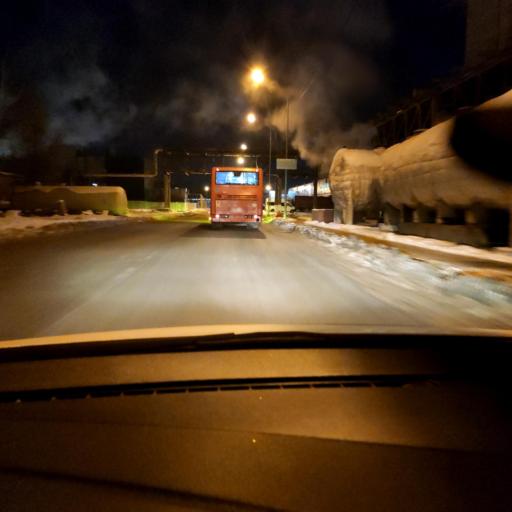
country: RU
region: Tatarstan
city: Staroye Arakchino
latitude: 55.8301
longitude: 49.0434
